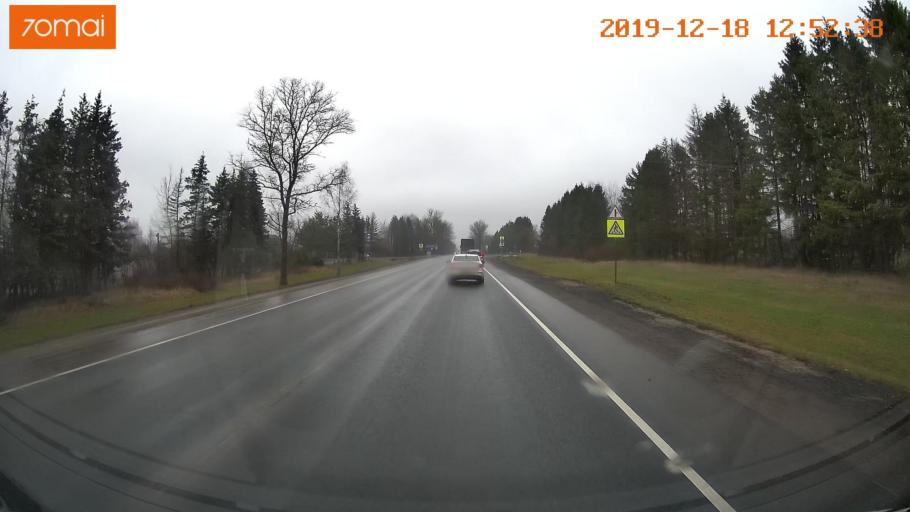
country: RU
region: Moskovskaya
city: Klin
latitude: 56.3128
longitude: 36.6888
